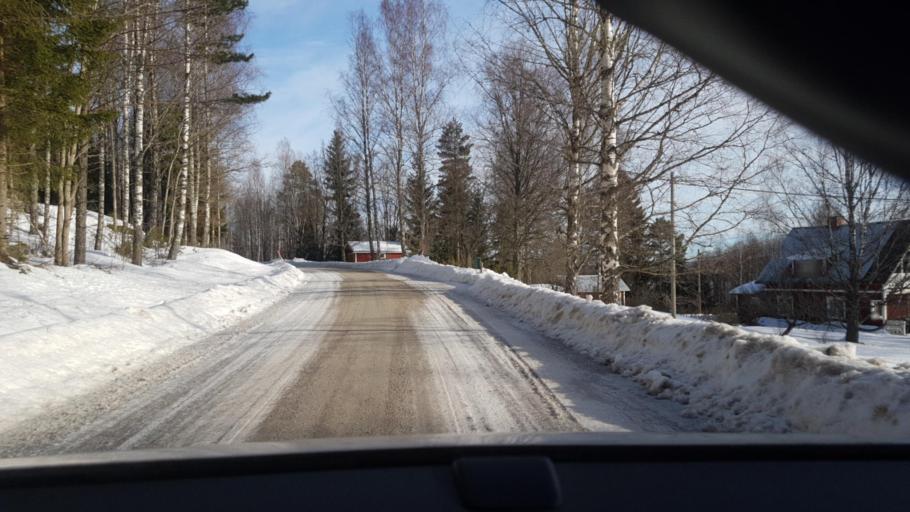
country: SE
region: Vaermland
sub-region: Eda Kommun
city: Amotfors
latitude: 59.7356
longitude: 12.2786
